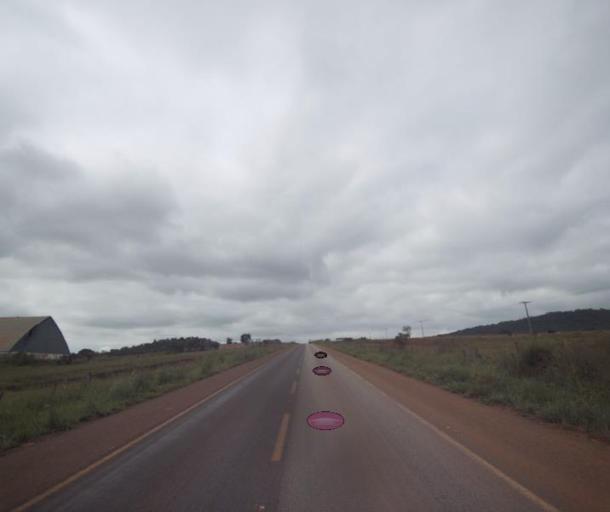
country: BR
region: Goias
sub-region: Barro Alto
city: Barro Alto
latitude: -14.9596
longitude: -48.9317
